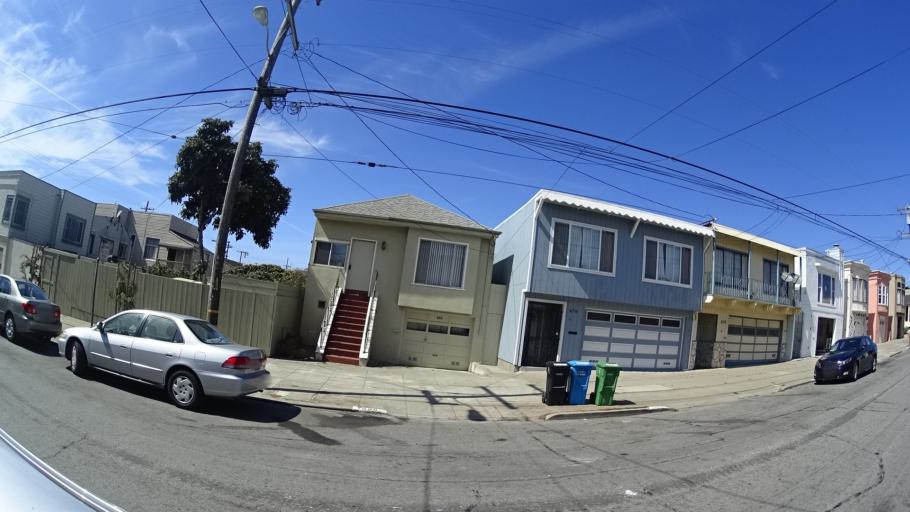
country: US
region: California
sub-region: San Mateo County
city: Daly City
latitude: 37.7173
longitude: -122.4318
